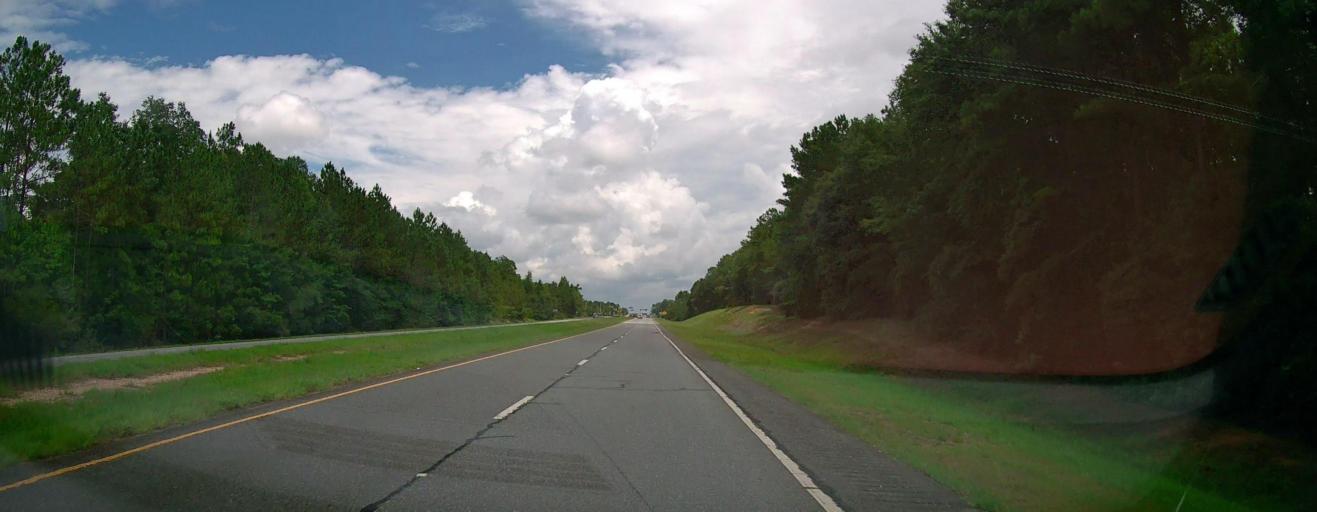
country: US
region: Georgia
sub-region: Dodge County
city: Eastman
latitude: 32.1787
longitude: -83.1878
